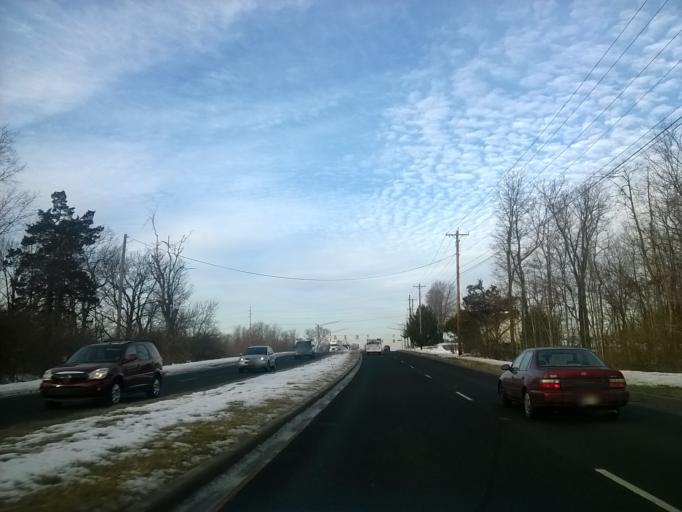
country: US
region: Indiana
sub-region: Hamilton County
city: Carmel
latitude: 40.0003
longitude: -86.0869
